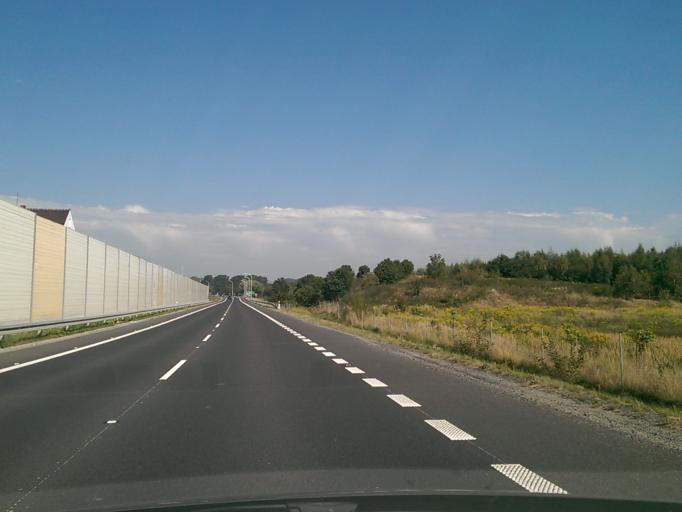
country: DE
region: Saxony
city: Zittau
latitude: 50.8963
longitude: 14.8500
